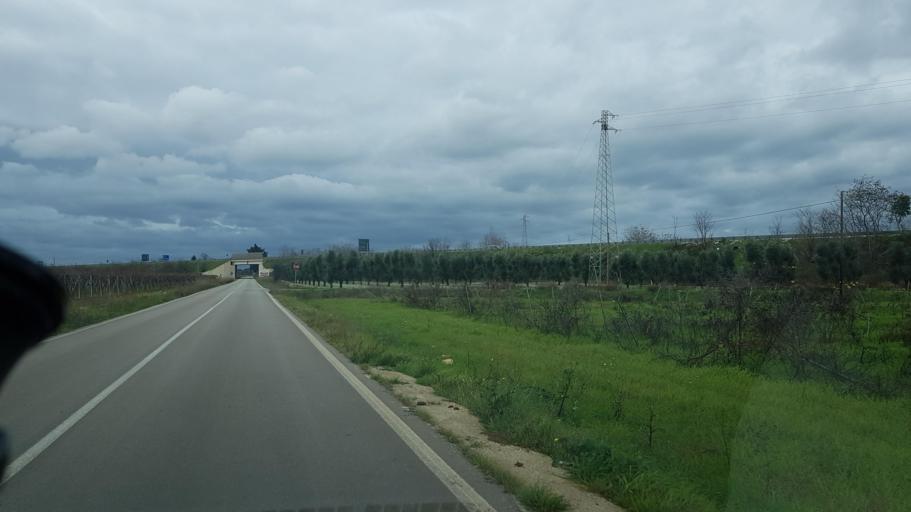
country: IT
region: Apulia
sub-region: Provincia di Brindisi
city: Francavilla Fontana
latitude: 40.5455
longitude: 17.5521
